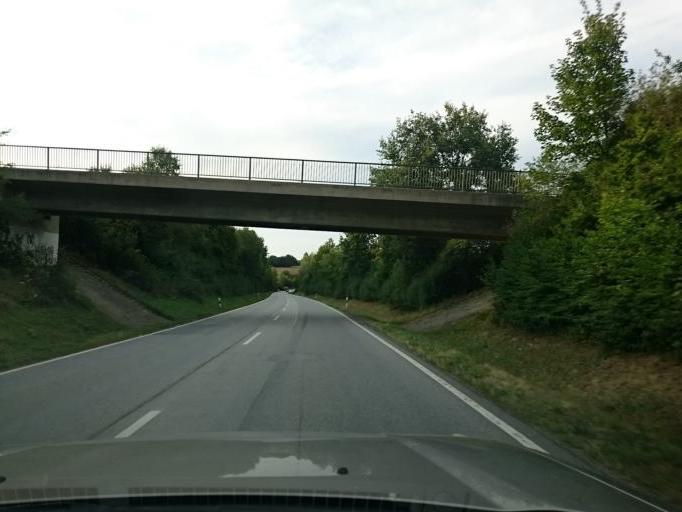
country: DE
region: Bavaria
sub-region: Lower Bavaria
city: Simbach
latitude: 48.5626
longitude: 12.7315
